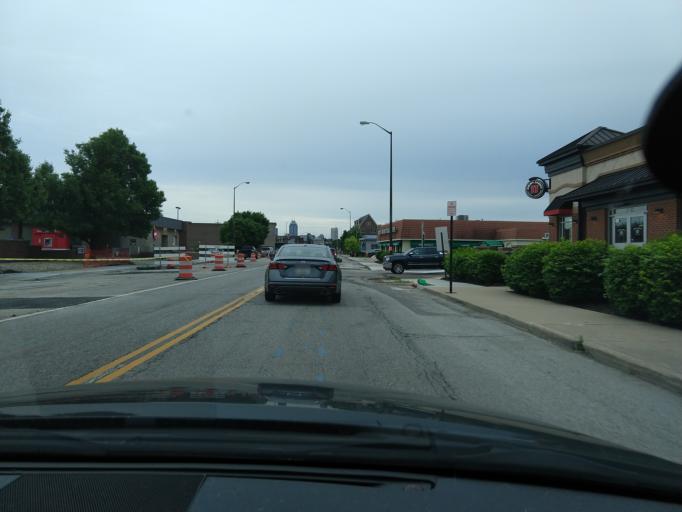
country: US
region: Indiana
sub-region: Marion County
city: Indianapolis
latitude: 39.8007
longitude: -86.1569
